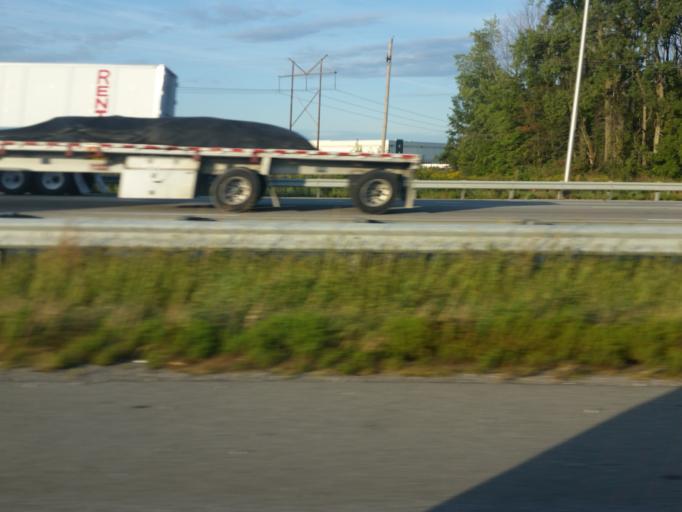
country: US
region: Indiana
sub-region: Boone County
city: Dale
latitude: 39.9770
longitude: -86.3904
